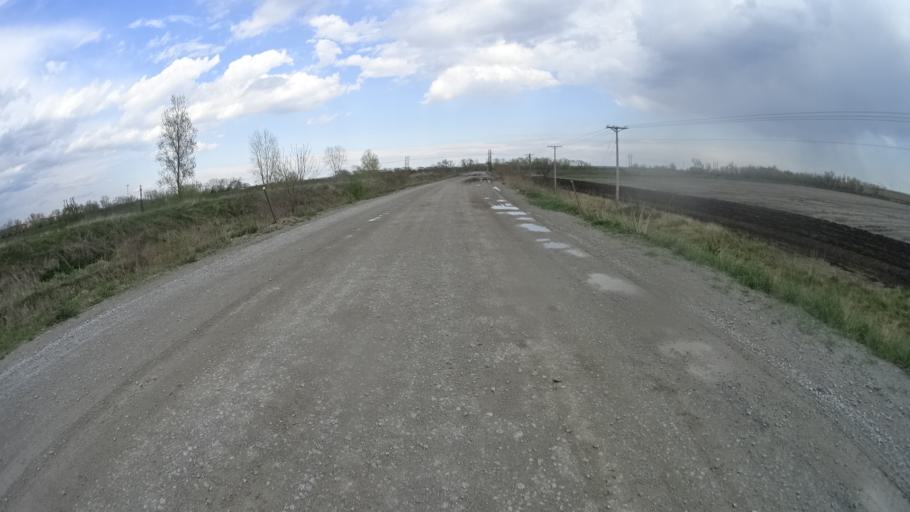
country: US
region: Nebraska
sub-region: Sarpy County
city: Offutt Air Force Base
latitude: 41.1038
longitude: -95.9230
